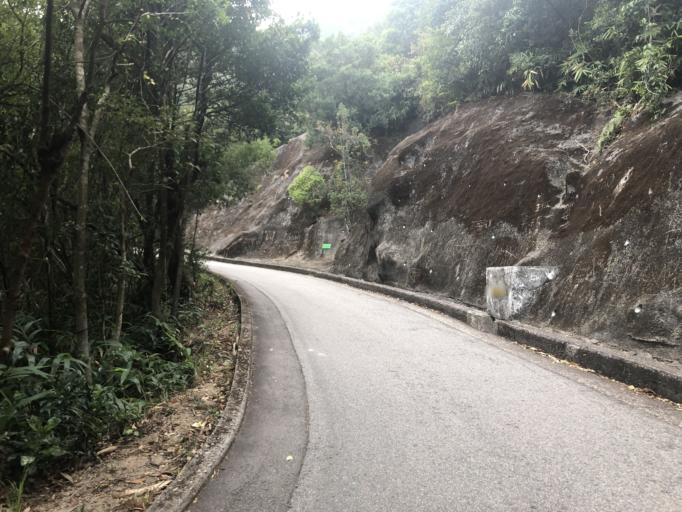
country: HK
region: Wanchai
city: Wan Chai
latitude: 22.2773
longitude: 114.2088
